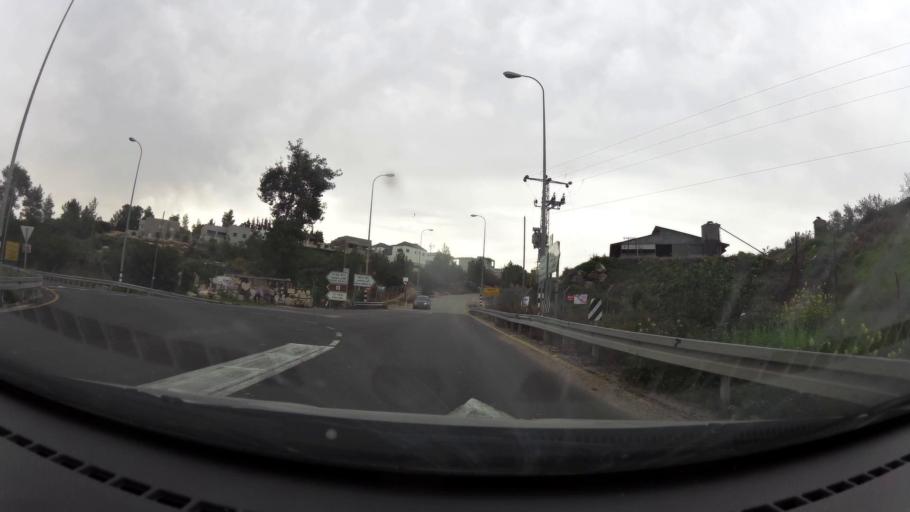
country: PS
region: West Bank
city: Surif
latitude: 31.6734
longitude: 35.0116
